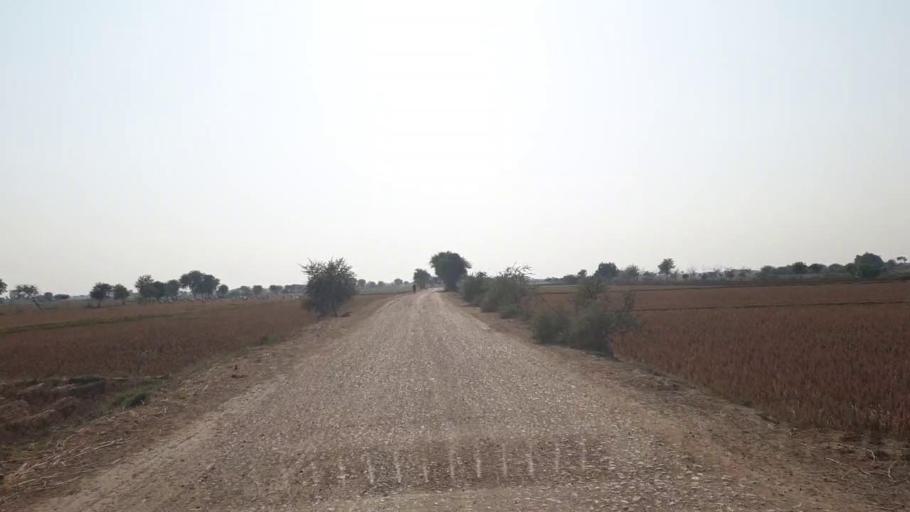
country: PK
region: Sindh
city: Matli
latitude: 24.9454
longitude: 68.6822
